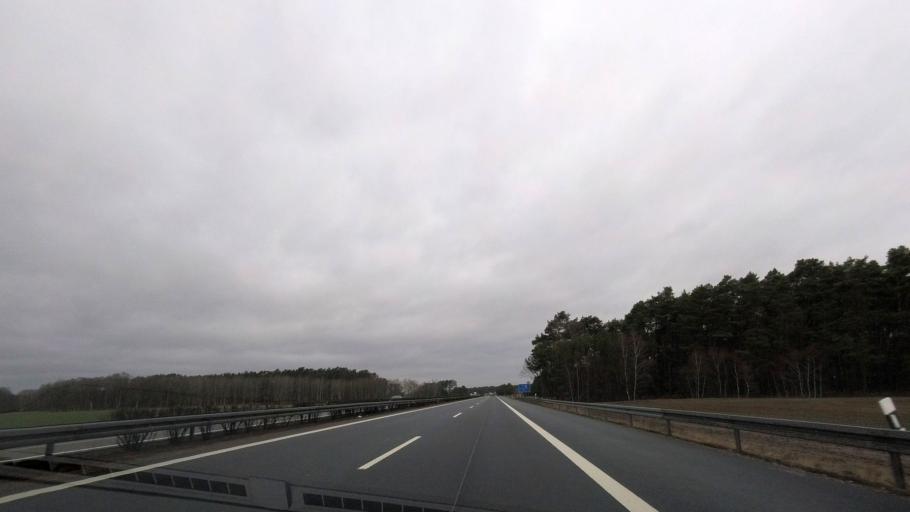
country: DE
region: Mecklenburg-Vorpommern
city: Sulstorf
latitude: 53.4568
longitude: 11.3543
